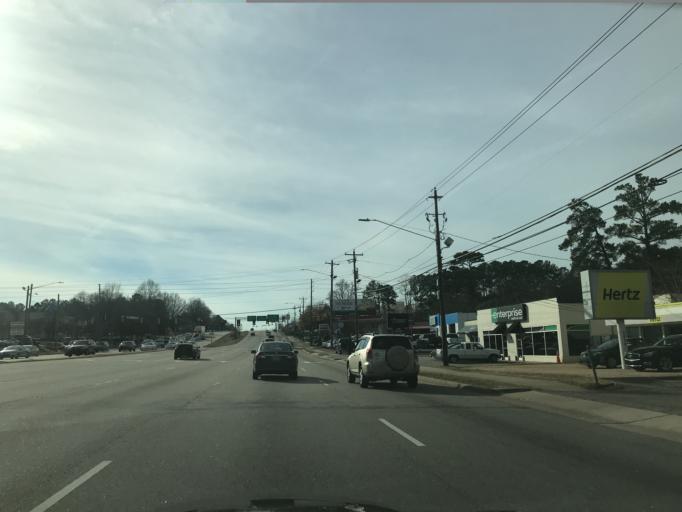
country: US
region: North Carolina
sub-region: Wake County
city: Raleigh
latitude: 35.8196
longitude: -78.5947
